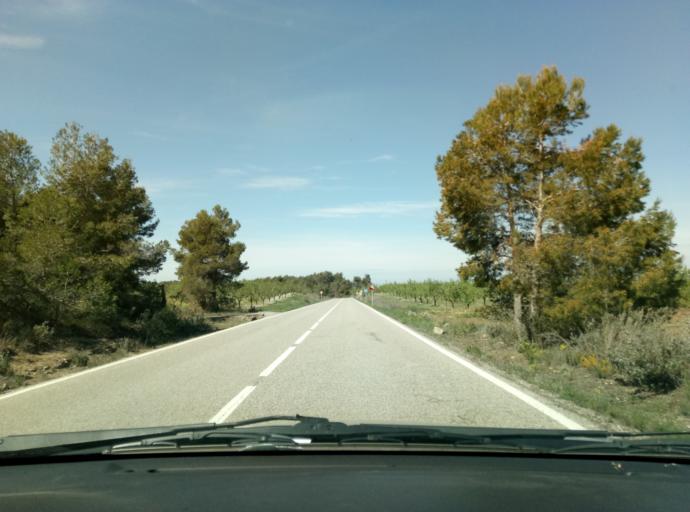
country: ES
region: Catalonia
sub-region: Provincia de Lleida
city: Fulleda
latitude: 41.5038
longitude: 1.0087
